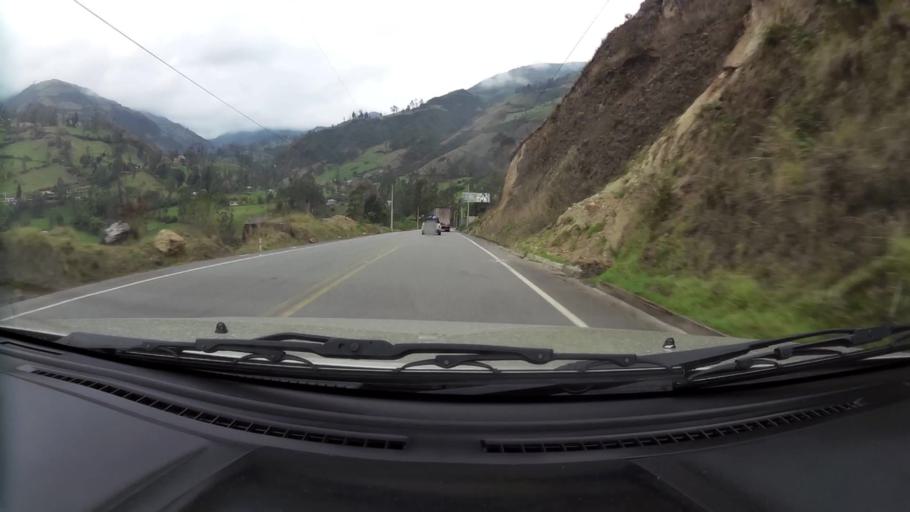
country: EC
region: Chimborazo
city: Alausi
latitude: -2.3082
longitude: -78.9111
